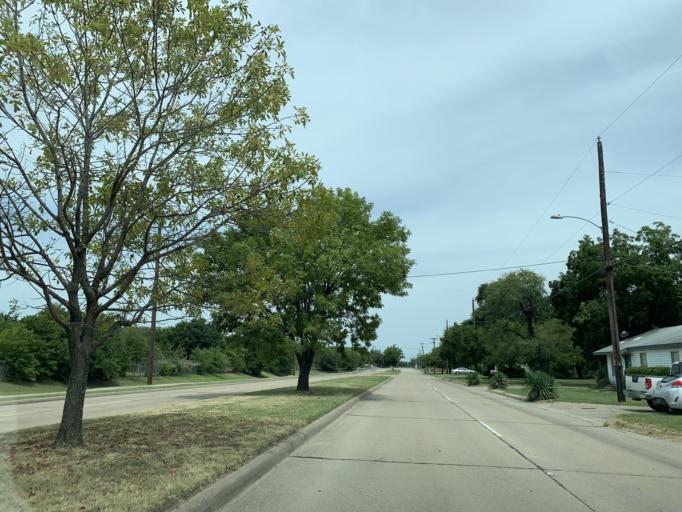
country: US
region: Texas
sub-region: Dallas County
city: Cedar Hill
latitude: 32.6530
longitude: -97.0148
